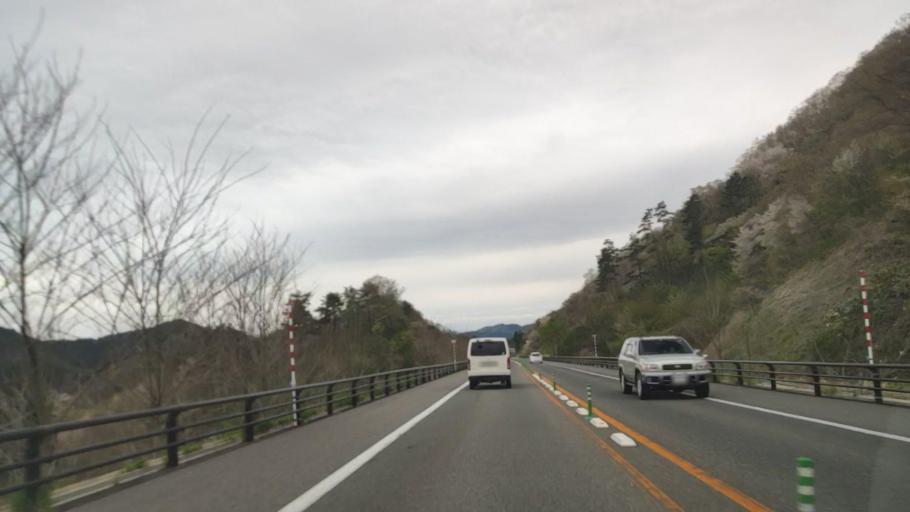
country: JP
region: Akita
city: Odate
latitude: 40.3209
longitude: 140.5942
